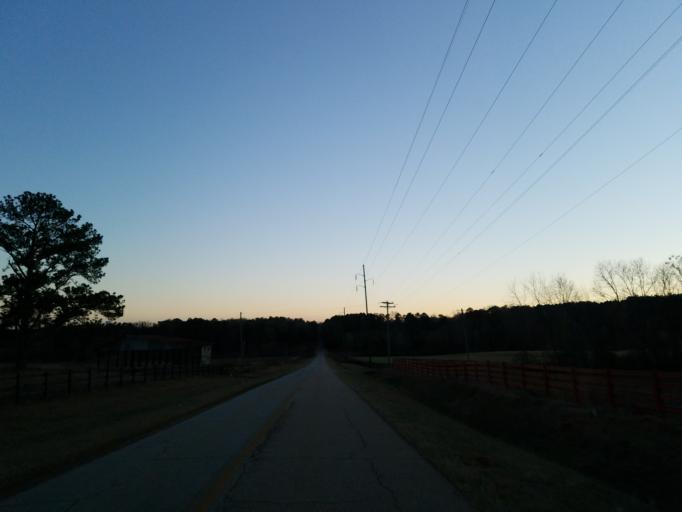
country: US
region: Georgia
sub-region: Monroe County
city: Forsyth
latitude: 32.9957
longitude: -83.8791
